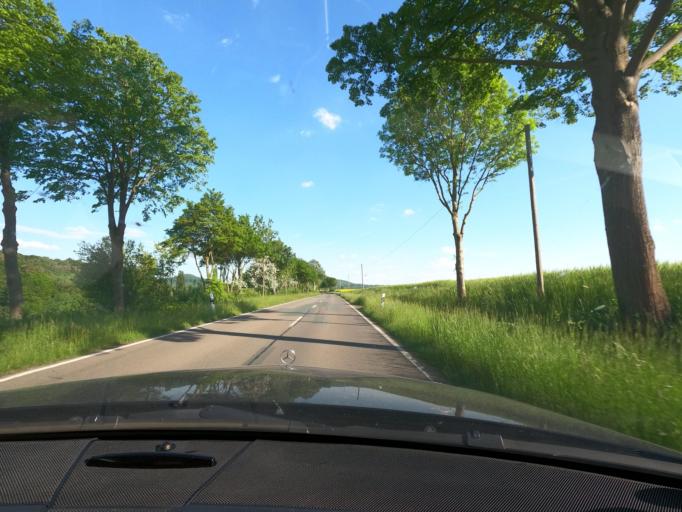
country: DE
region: Hesse
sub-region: Regierungsbezirk Kassel
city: Martinhagen
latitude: 51.3270
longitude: 9.2510
